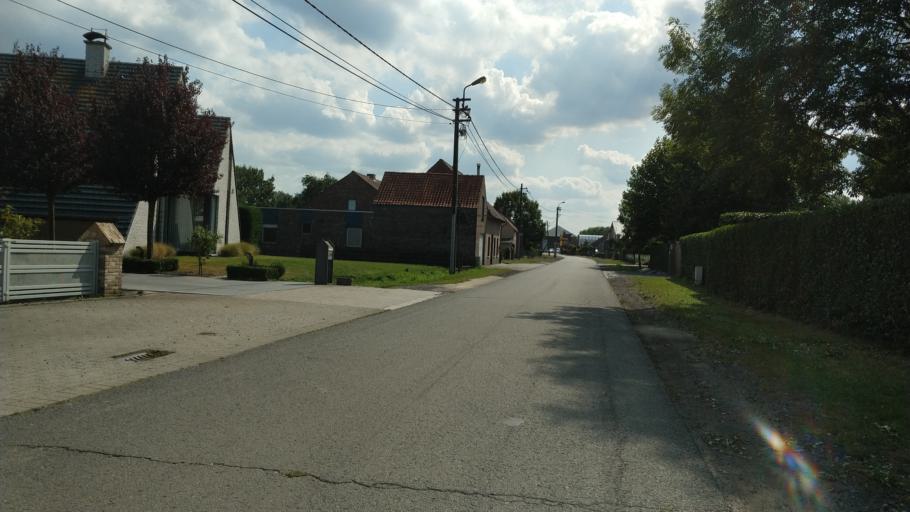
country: BE
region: Flanders
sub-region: Provincie Oost-Vlaanderen
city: Kaprijke
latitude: 51.1966
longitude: 3.6795
